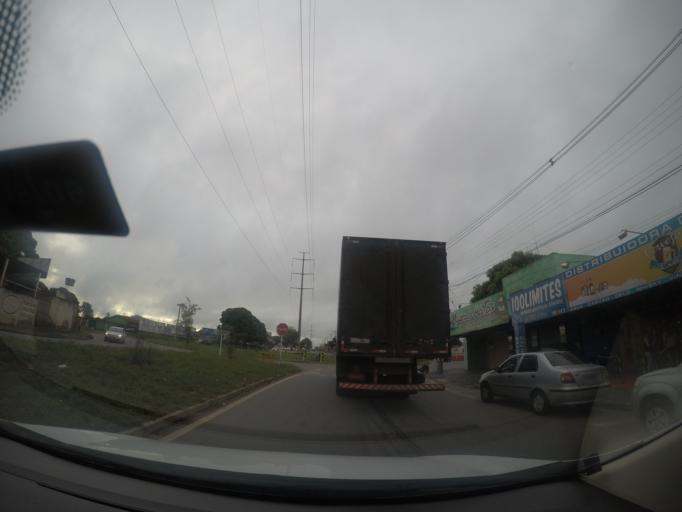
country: BR
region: Goias
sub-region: Aparecida De Goiania
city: Aparecida de Goiania
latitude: -16.7580
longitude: -49.3331
